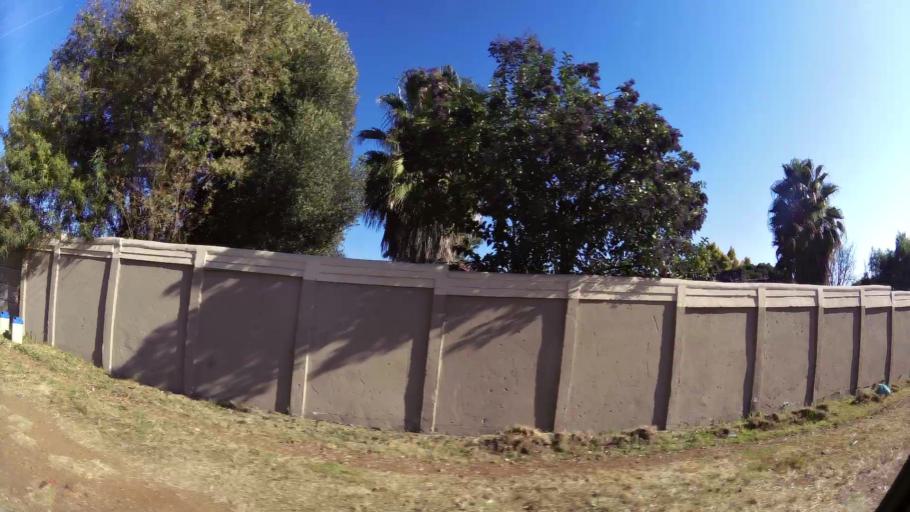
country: ZA
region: Gauteng
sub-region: Ekurhuleni Metropolitan Municipality
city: Germiston
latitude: -26.3470
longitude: 28.0918
